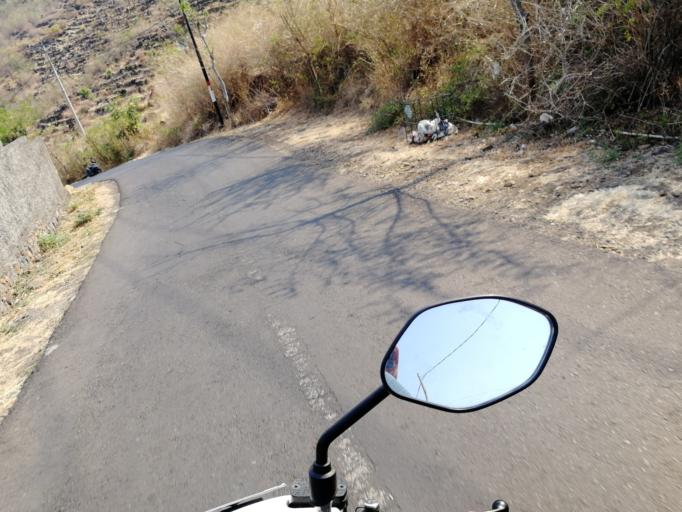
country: ID
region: Bali
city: Biaslantang Kaler
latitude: -8.3608
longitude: 115.6983
